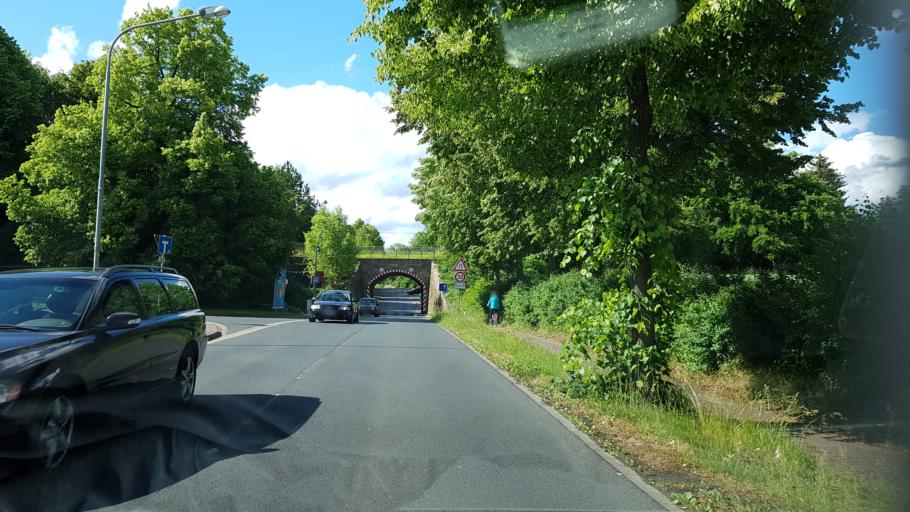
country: DE
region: Lower Saxony
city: Bovenden
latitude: 51.5876
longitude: 9.8717
